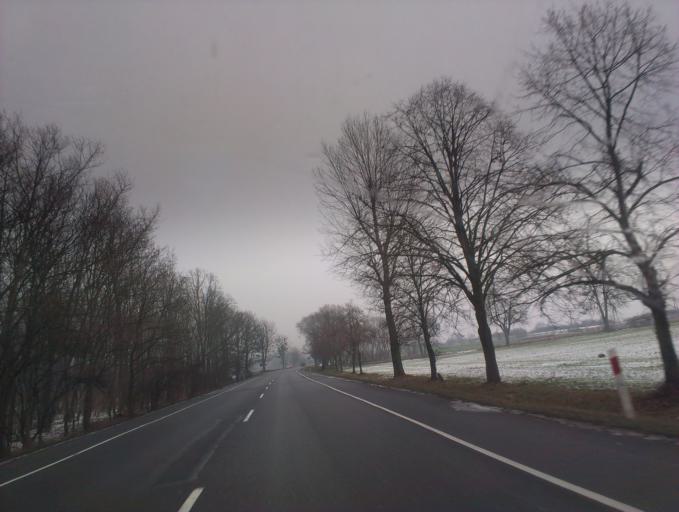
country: PL
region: Greater Poland Voivodeship
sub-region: Powiat obornicki
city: Oborniki
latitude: 52.6897
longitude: 16.8856
